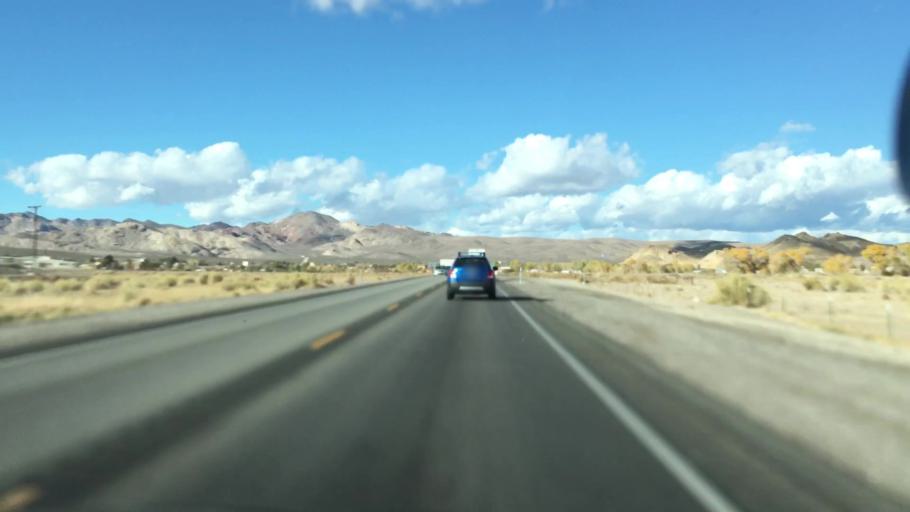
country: US
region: Nevada
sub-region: Nye County
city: Beatty
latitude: 36.8955
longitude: -116.7525
